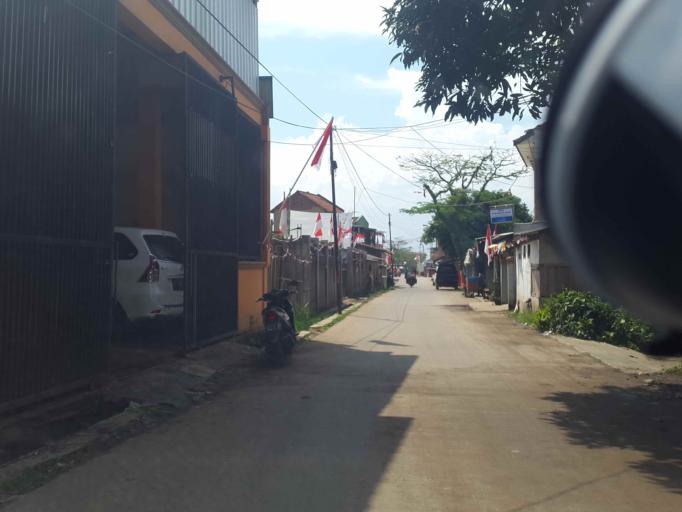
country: ID
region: West Java
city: Banjaran
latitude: -7.0437
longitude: 107.5632
